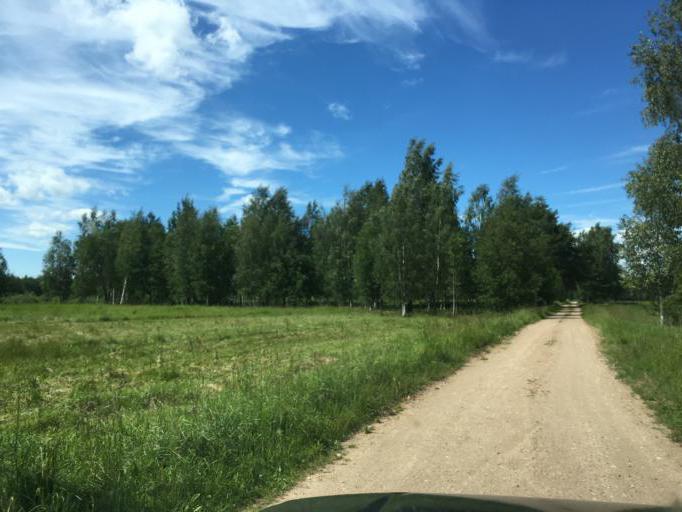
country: LV
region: Balvu Rajons
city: Balvi
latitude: 57.1555
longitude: 27.3200
